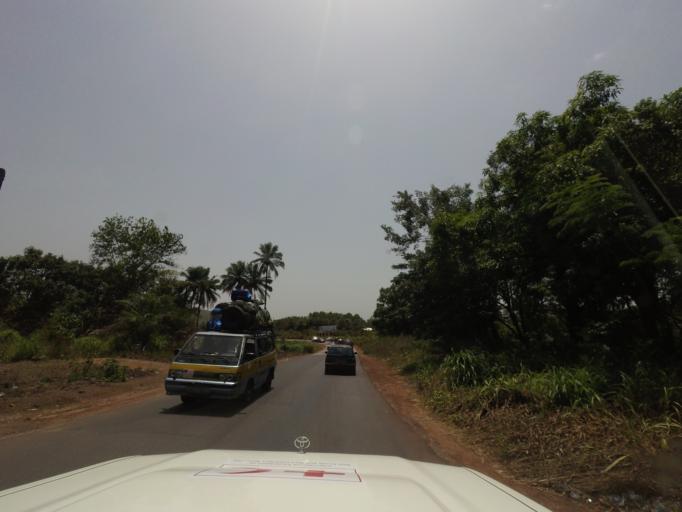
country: GN
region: Kindia
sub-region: Coyah
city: Coyah
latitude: 9.7816
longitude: -13.3398
